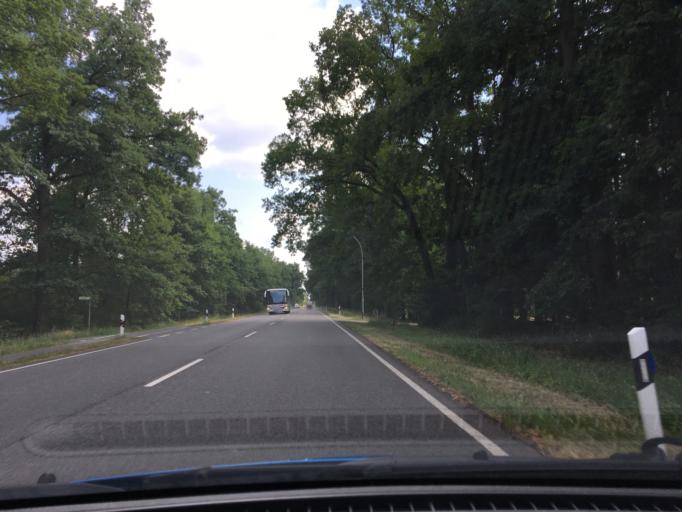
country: DE
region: Lower Saxony
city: Handeloh
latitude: 53.1953
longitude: 9.8292
